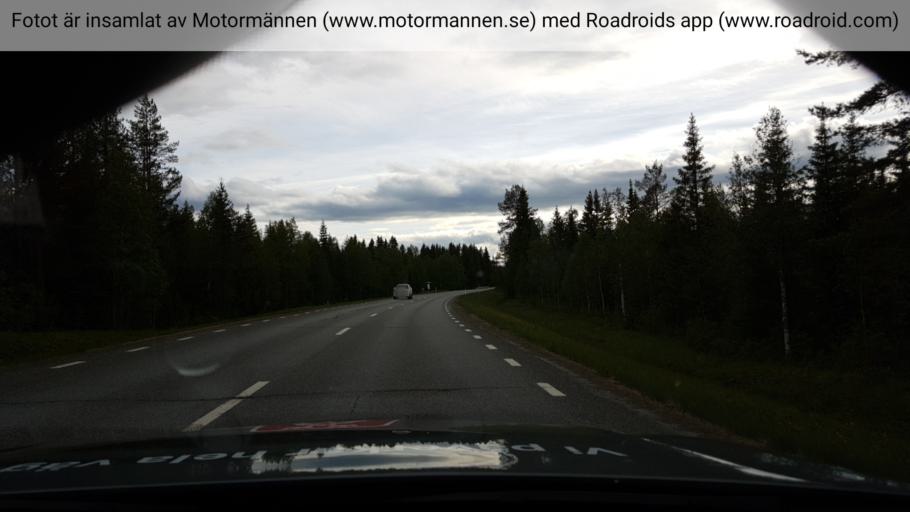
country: SE
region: Jaemtland
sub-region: OEstersunds Kommun
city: Lit
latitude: 63.4856
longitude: 15.2374
